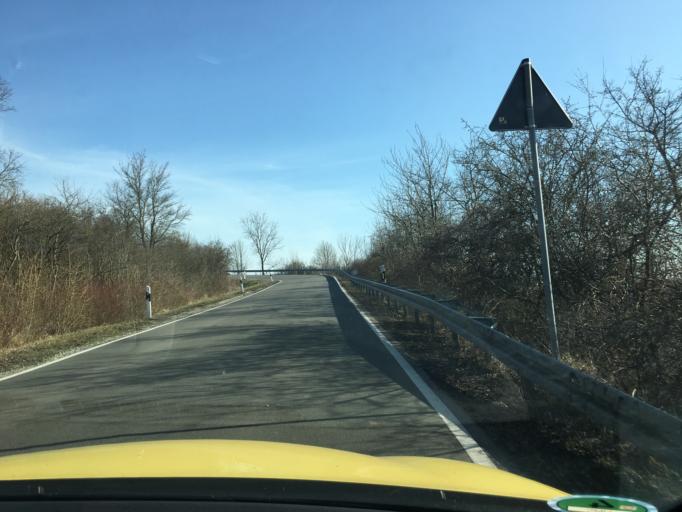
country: DE
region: Saxony-Anhalt
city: Laucha
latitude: 51.2397
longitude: 11.6986
